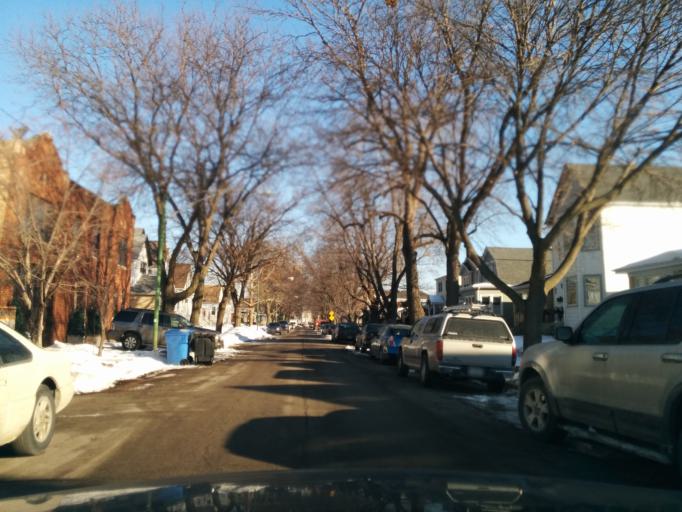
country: US
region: Illinois
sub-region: Cook County
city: Lincolnwood
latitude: 41.9546
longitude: -87.7418
